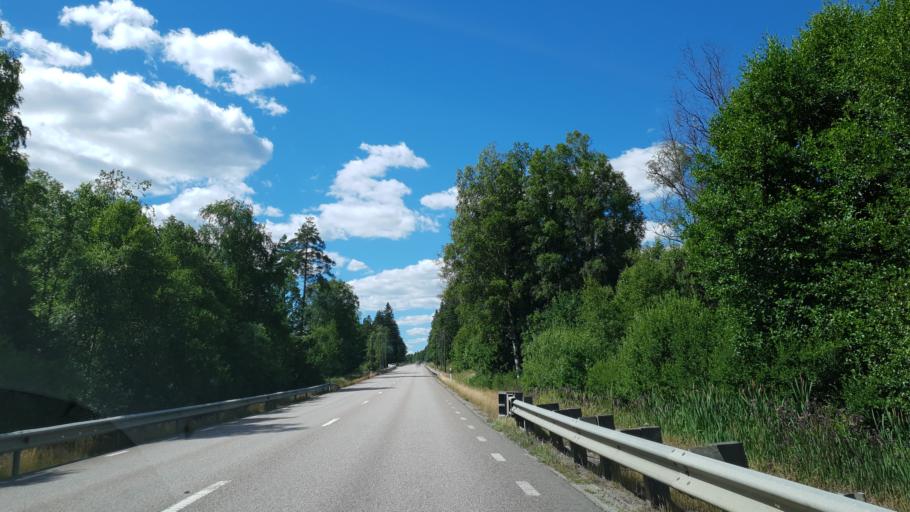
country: SE
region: Kronoberg
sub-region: Lessebo Kommun
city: Hovmantorp
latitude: 56.7829
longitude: 15.1971
